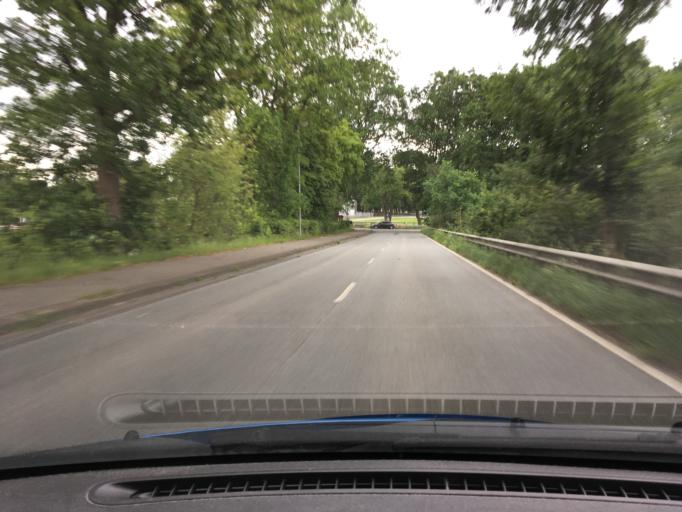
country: DE
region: Lower Saxony
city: Sittensen
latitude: 53.2893
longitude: 9.5001
